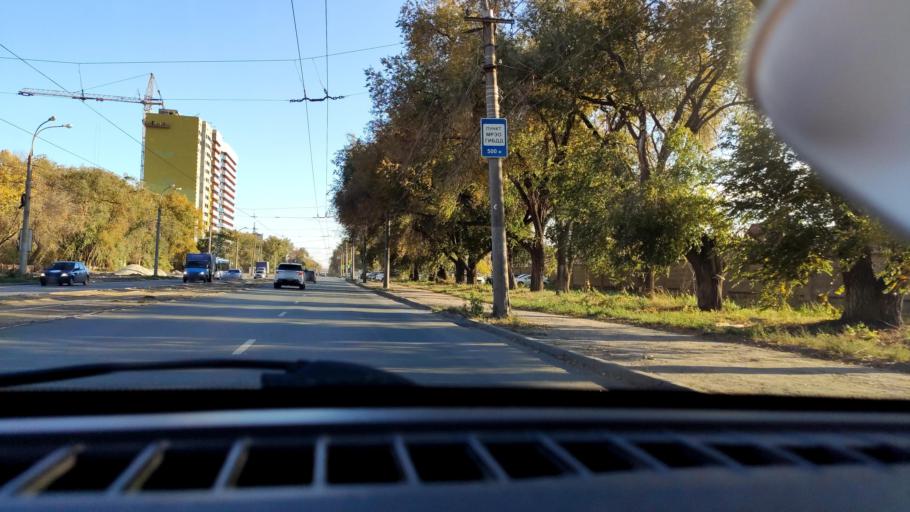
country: RU
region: Samara
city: Smyshlyayevka
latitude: 53.2040
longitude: 50.2808
